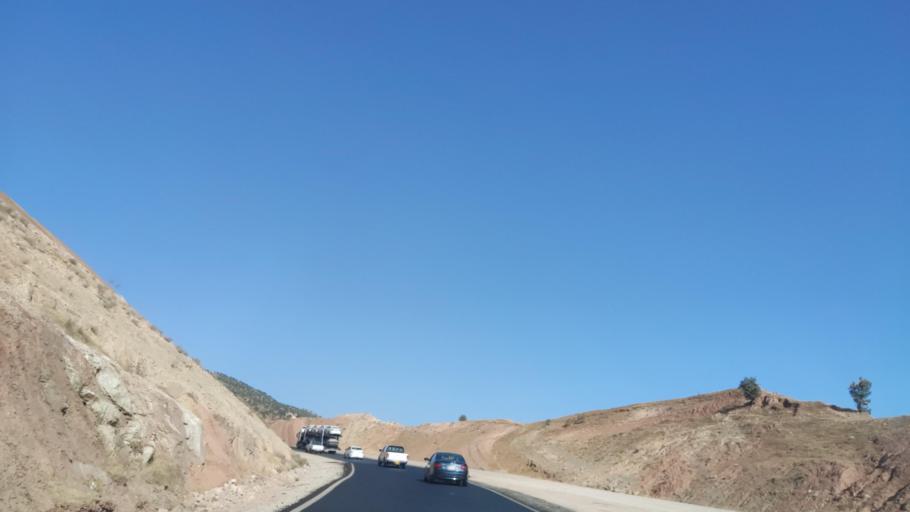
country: IQ
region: Arbil
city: Shaqlawah
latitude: 36.4348
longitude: 44.3001
